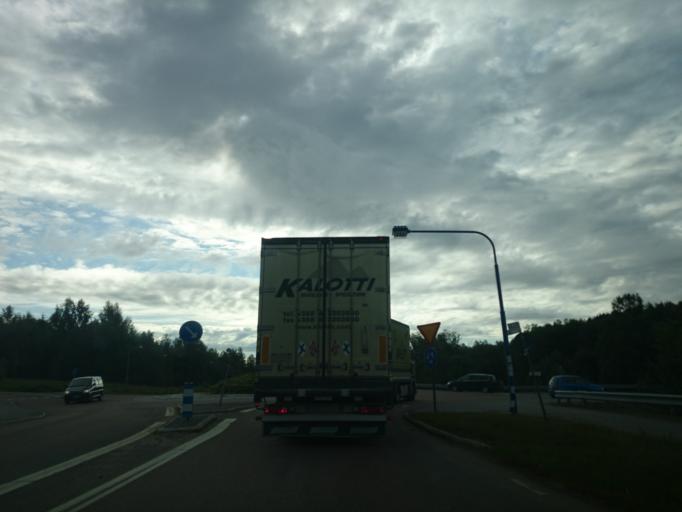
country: SE
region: Vaesternorrland
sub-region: Sundsvalls Kommun
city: Johannedal
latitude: 62.4128
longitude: 17.3673
